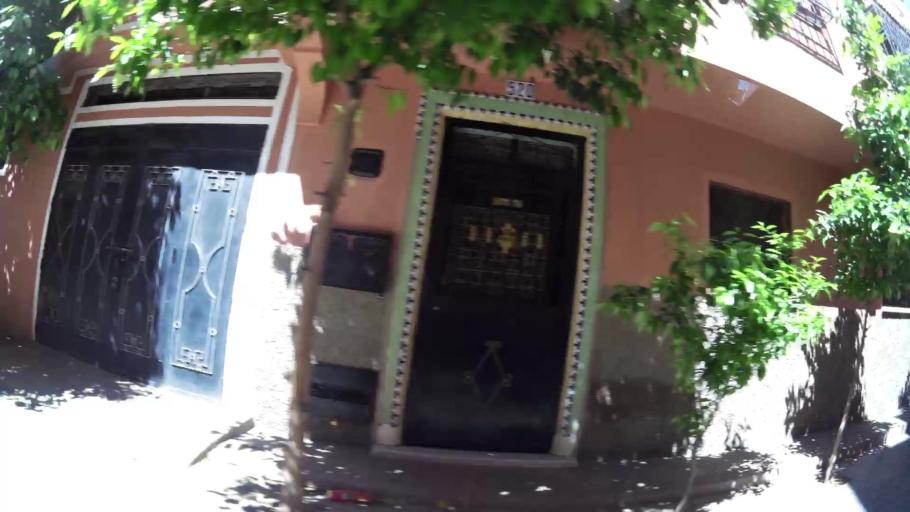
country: MA
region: Marrakech-Tensift-Al Haouz
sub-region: Marrakech
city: Marrakesh
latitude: 31.6308
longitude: -8.0690
